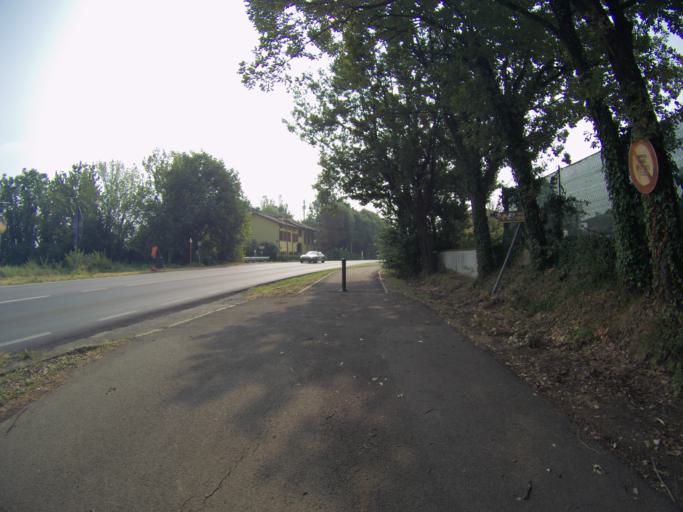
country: IT
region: Emilia-Romagna
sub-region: Provincia di Reggio Emilia
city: Borzano
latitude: 44.6102
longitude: 10.6365
